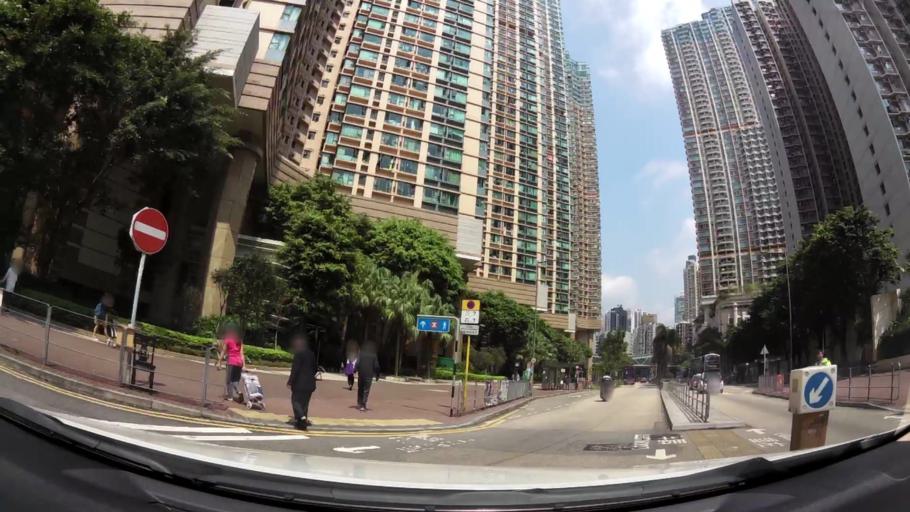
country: HK
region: Sham Shui Po
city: Sham Shui Po
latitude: 22.3158
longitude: 114.1638
